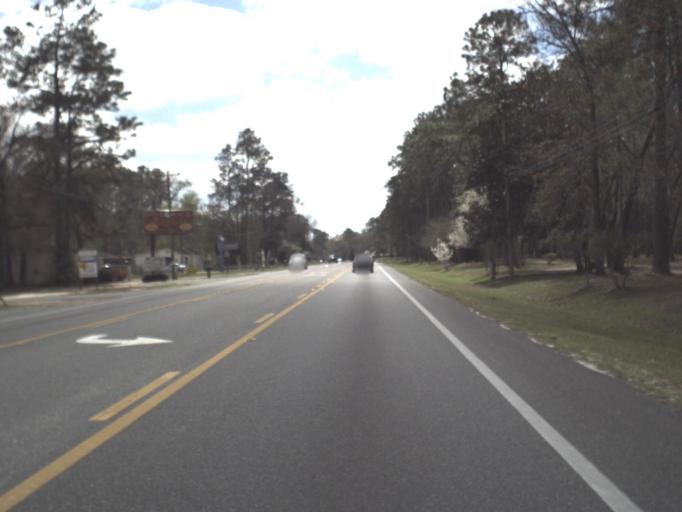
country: US
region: Florida
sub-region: Wakulla County
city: Crawfordville
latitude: 30.1893
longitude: -84.3732
